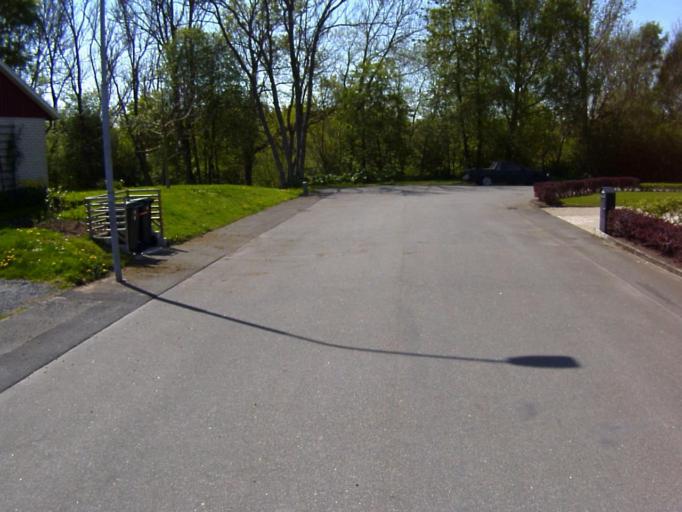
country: SE
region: Skane
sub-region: Kristianstads Kommun
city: Onnestad
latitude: 55.9293
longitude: 13.9883
